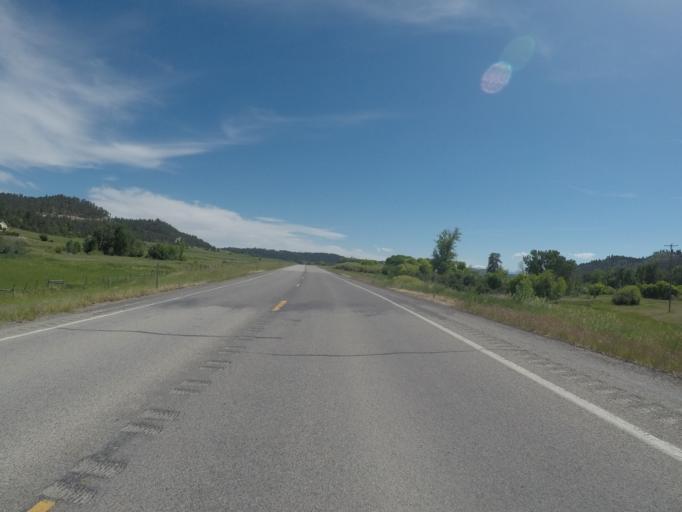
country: US
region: Montana
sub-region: Stillwater County
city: Columbus
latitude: 45.6296
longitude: -109.2786
